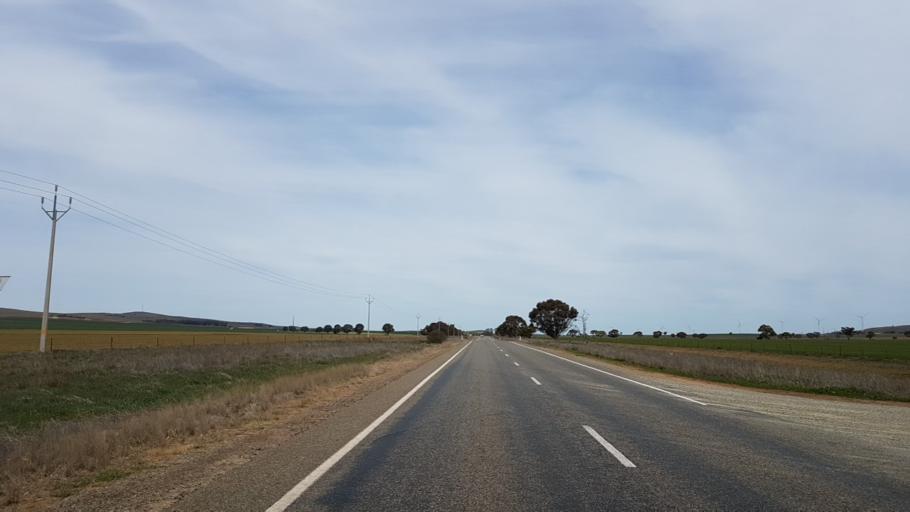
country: AU
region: South Australia
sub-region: Northern Areas
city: Jamestown
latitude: -33.0709
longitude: 138.6160
